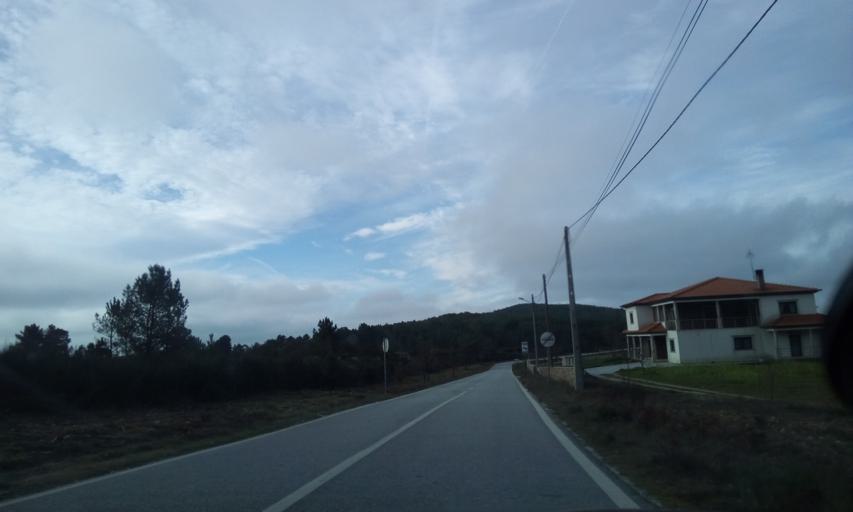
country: PT
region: Guarda
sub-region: Aguiar da Beira
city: Aguiar da Beira
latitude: 40.7761
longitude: -7.5184
